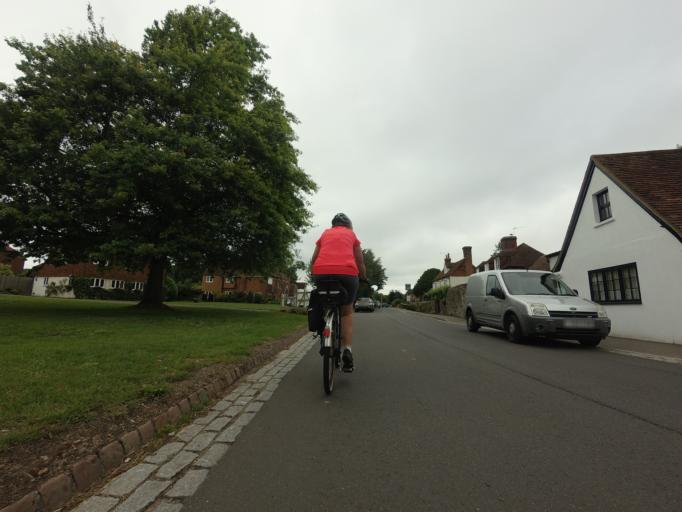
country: GB
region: England
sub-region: Kent
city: Kings Hill
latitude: 51.2909
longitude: 0.3745
